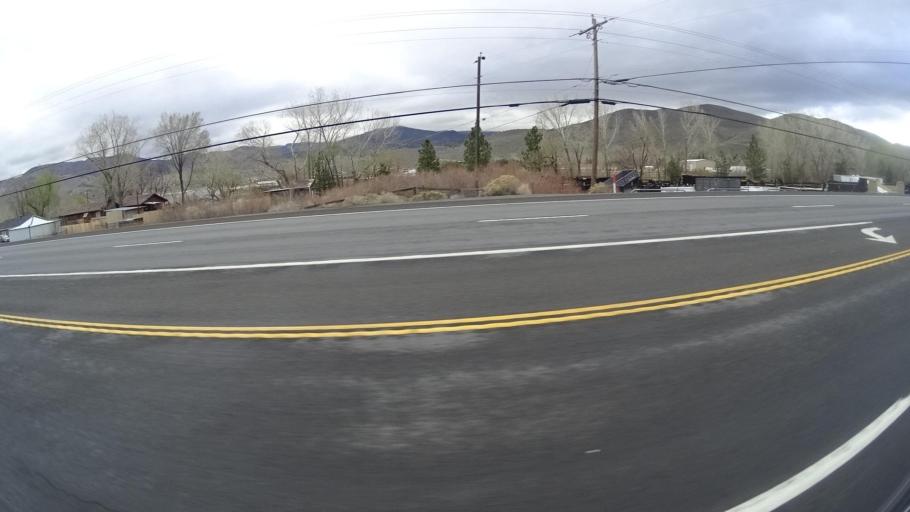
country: US
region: Nevada
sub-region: Storey County
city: Virginia City
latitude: 39.3706
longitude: -119.7479
